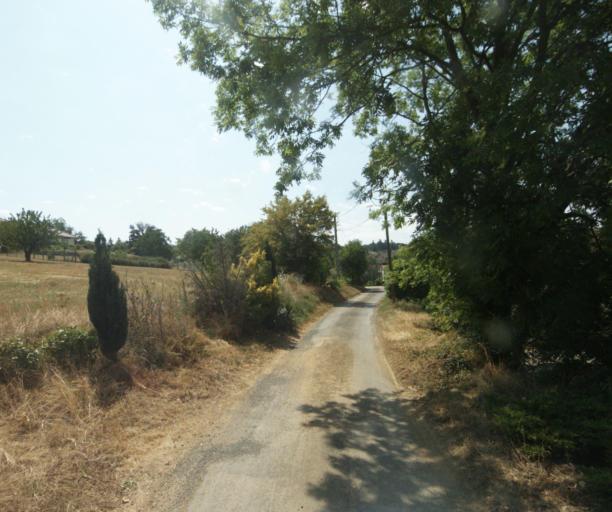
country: FR
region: Rhone-Alpes
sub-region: Departement du Rhone
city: Saint-Germain-Nuelles
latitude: 45.8322
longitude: 4.6235
